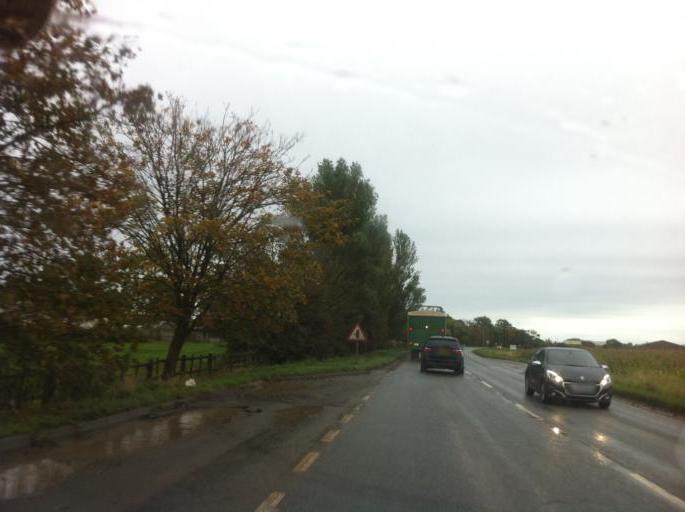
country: GB
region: England
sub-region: Lincolnshire
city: Boston
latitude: 53.0299
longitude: 0.1041
